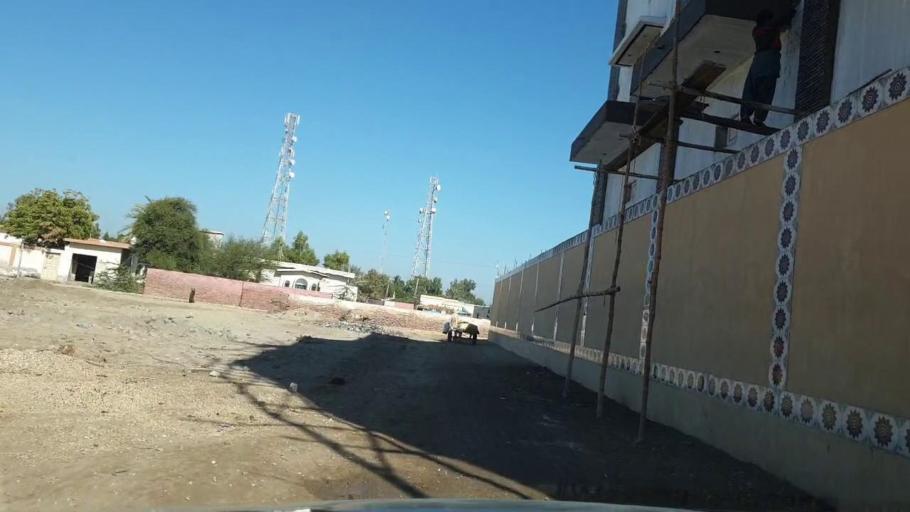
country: PK
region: Sindh
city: Tando Mittha Khan
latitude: 25.7985
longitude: 69.0691
